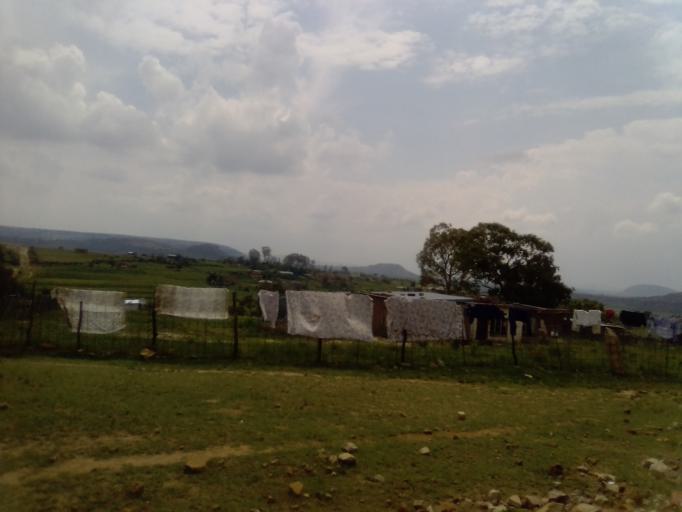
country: LS
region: Leribe
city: Leribe
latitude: -29.0250
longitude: 28.0166
